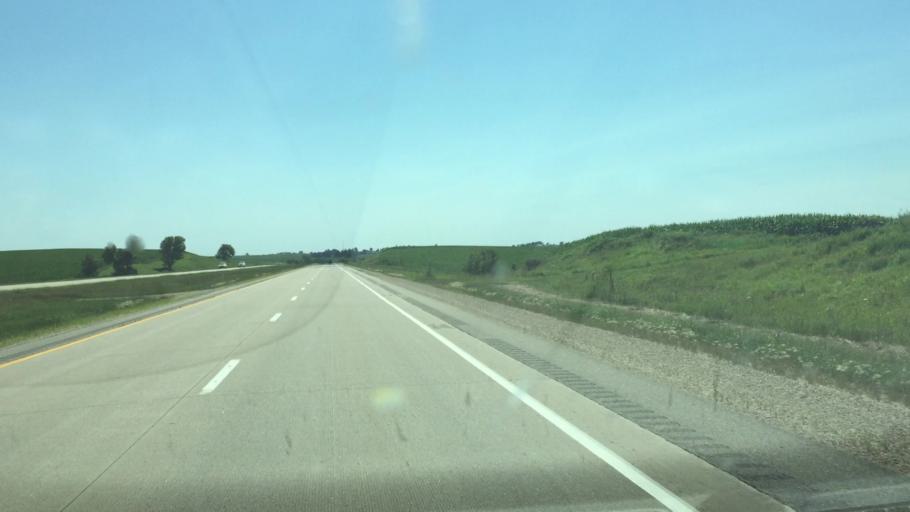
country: US
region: Iowa
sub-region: Dubuque County
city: Peosta
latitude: 42.3548
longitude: -90.8206
